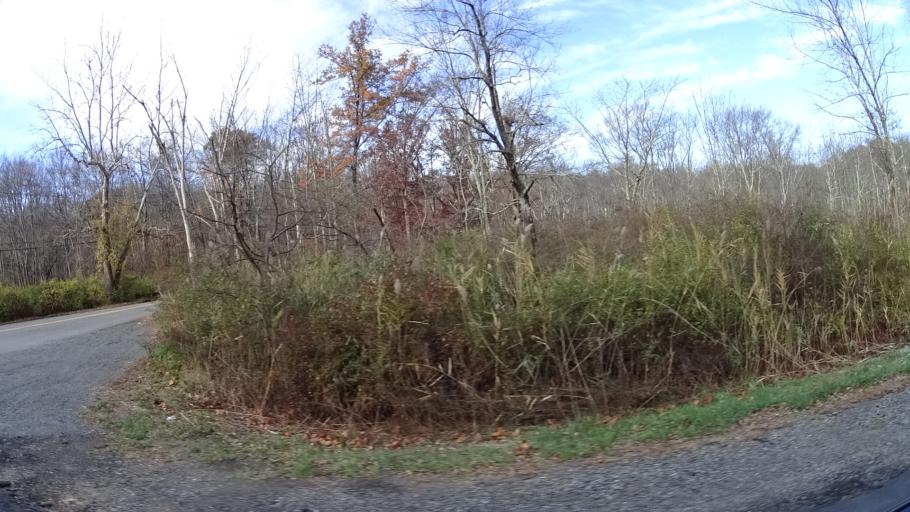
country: US
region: New Jersey
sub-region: Morris County
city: Mendham
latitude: 40.7885
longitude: -74.5511
